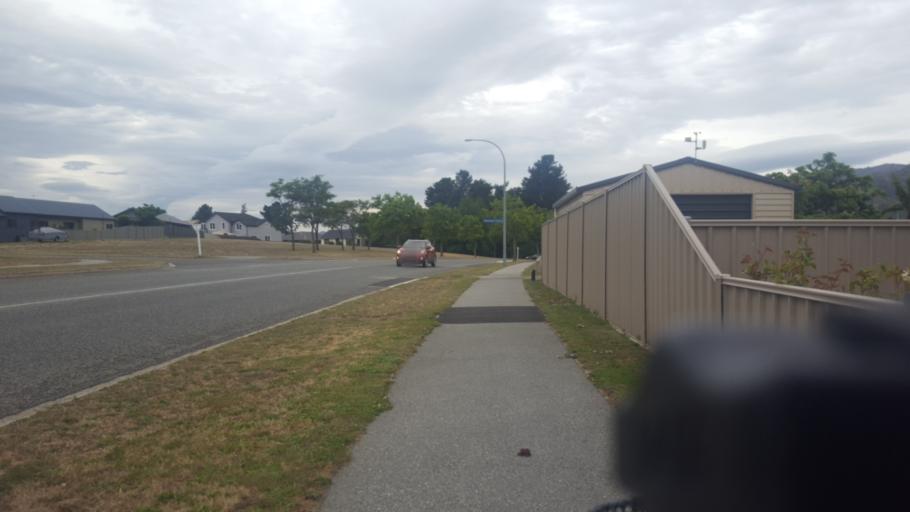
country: NZ
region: Otago
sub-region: Queenstown-Lakes District
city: Wanaka
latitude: -45.0456
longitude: 169.1885
